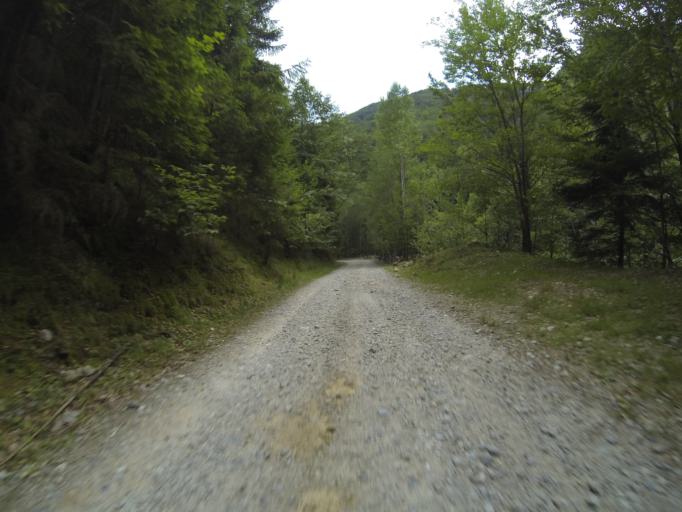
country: RO
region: Gorj
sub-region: Comuna Polovragi
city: Polovragi
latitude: 45.2319
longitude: 23.7709
